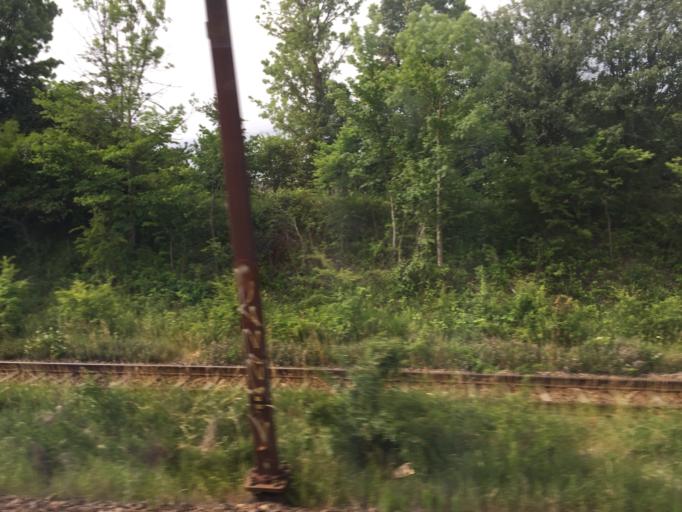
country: DK
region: South Denmark
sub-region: Odense Kommune
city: Odense
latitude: 55.4015
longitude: 10.3713
